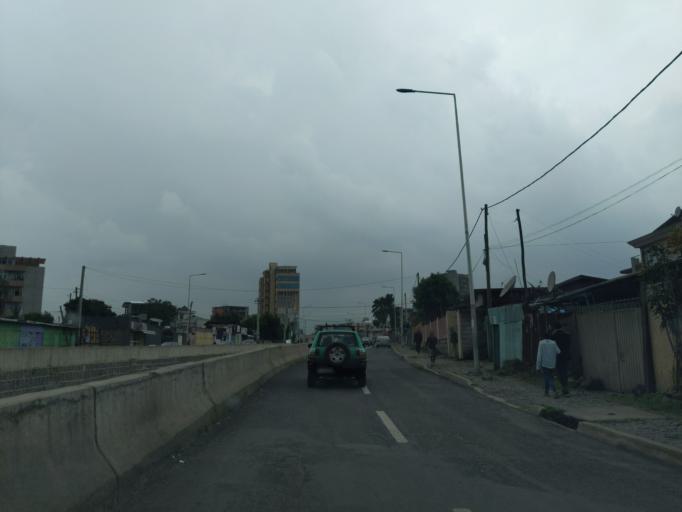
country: ET
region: Adis Abeba
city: Addis Ababa
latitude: 8.9849
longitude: 38.7655
